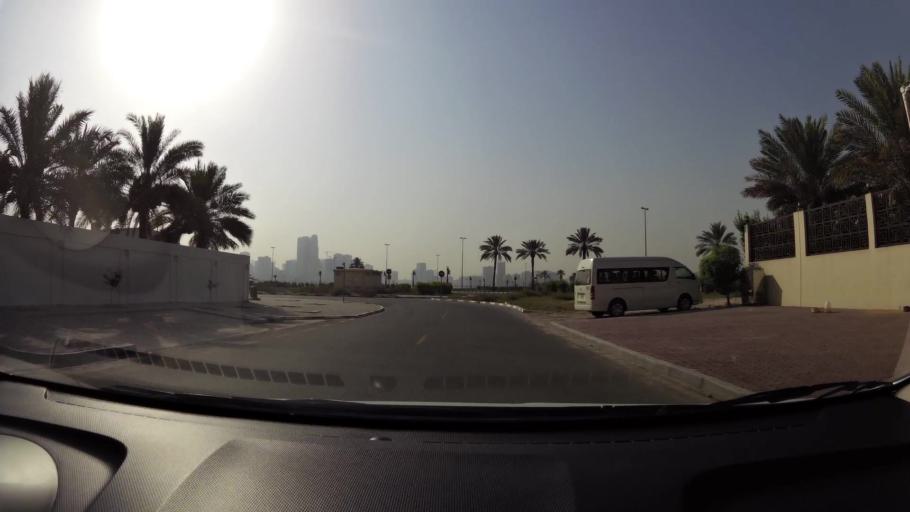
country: AE
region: Ash Shariqah
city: Sharjah
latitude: 25.3077
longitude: 55.3451
